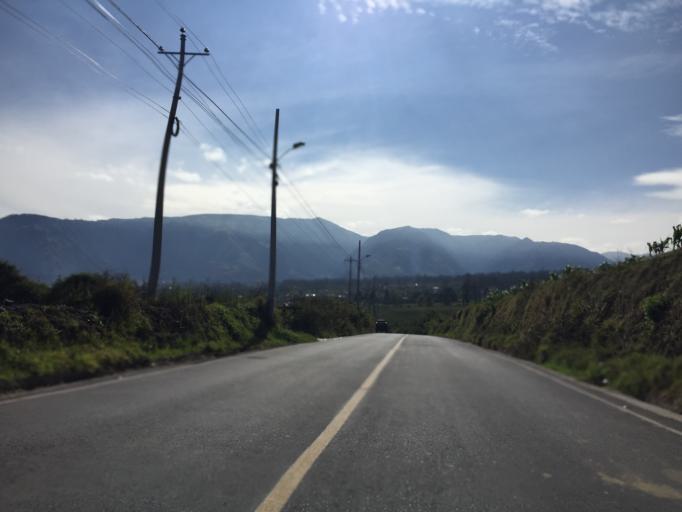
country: EC
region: Imbabura
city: Ibarra
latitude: 0.3178
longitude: -78.1532
